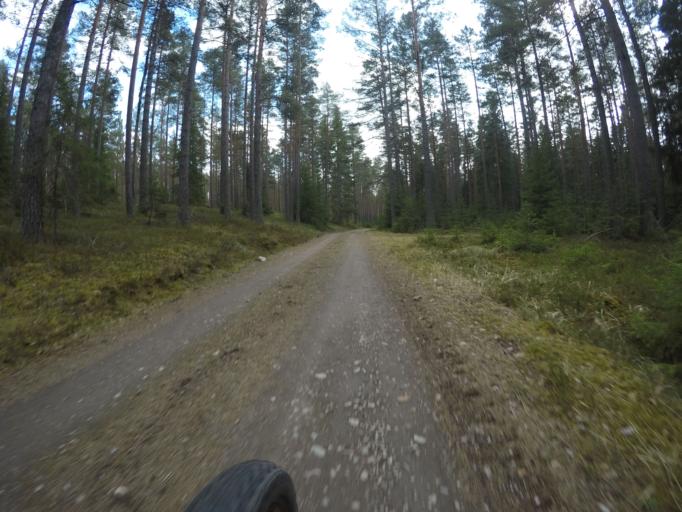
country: SE
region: Vaestmanland
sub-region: Kungsors Kommun
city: Kungsoer
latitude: 59.3412
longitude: 16.1071
